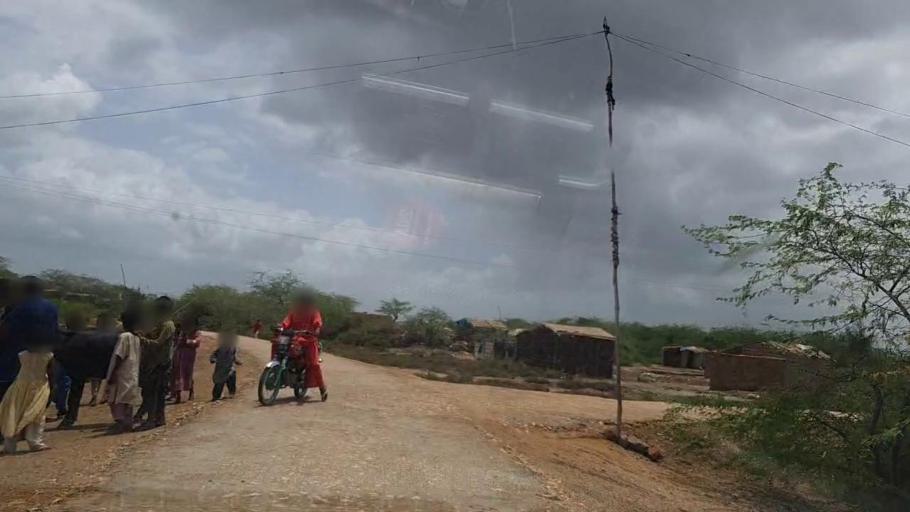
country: PK
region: Sindh
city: Thatta
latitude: 24.6208
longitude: 68.0263
